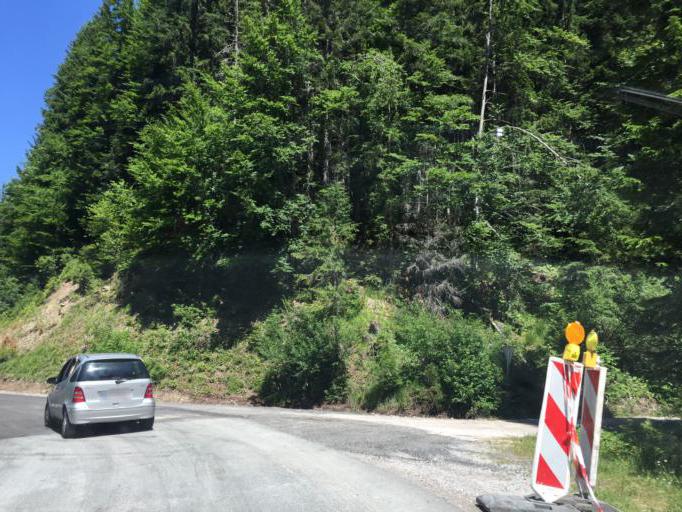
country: SI
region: Gorje
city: Zgornje Gorje
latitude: 46.3499
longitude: 13.9939
